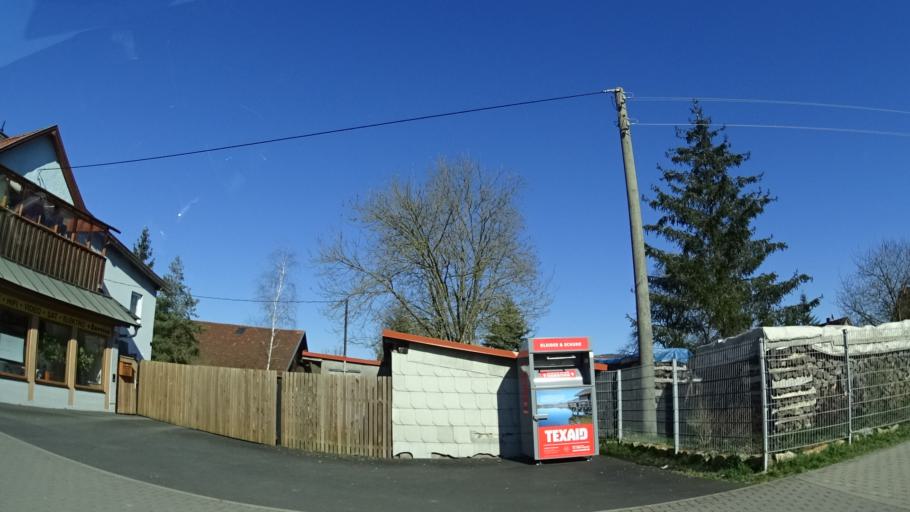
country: DE
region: Thuringia
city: Romhild
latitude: 50.4042
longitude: 10.5388
